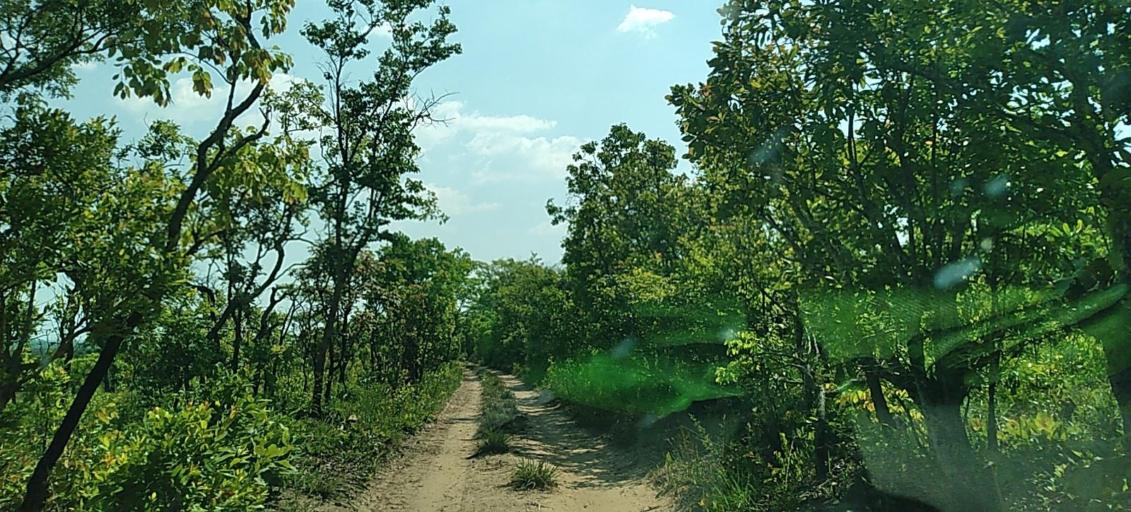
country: CD
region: Katanga
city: Kolwezi
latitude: -11.2659
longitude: 25.0000
